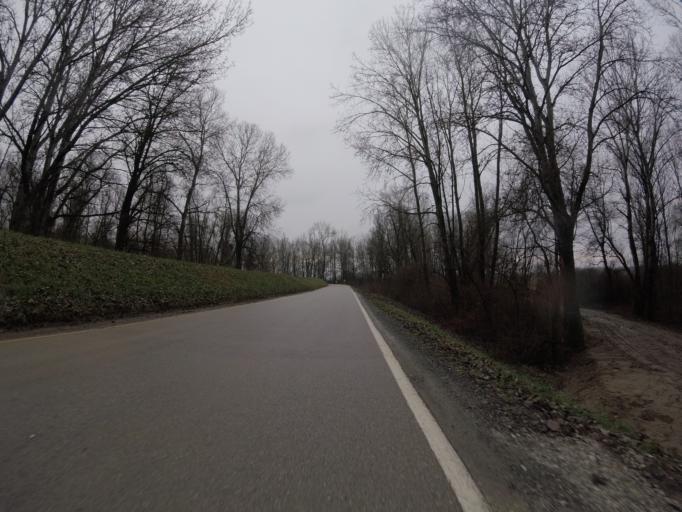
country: HR
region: Zagrebacka
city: Kuce
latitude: 45.6996
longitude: 16.2123
